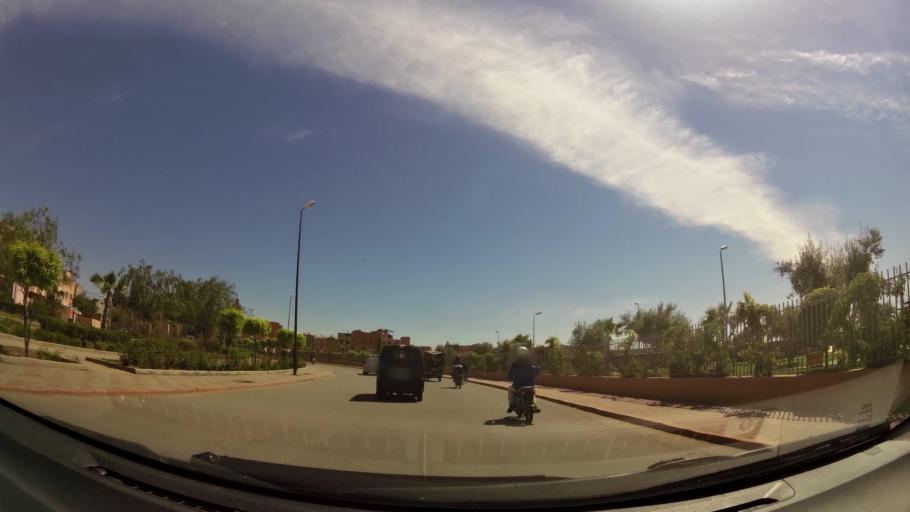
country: MA
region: Marrakech-Tensift-Al Haouz
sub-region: Marrakech
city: Marrakesh
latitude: 31.6010
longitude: -7.9618
